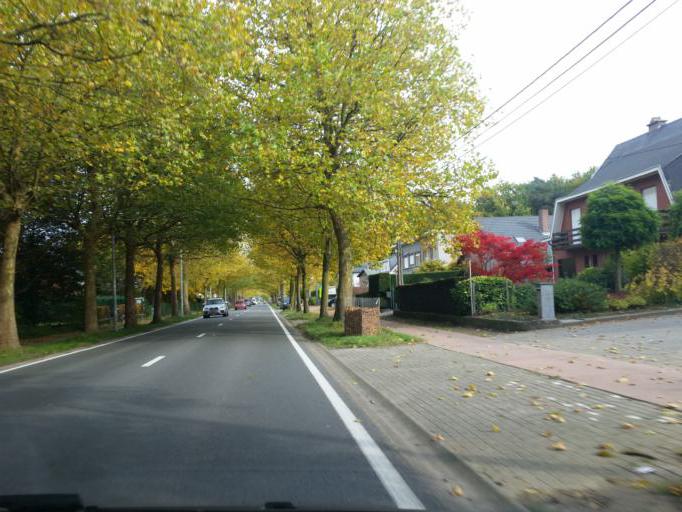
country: BE
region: Flanders
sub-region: Provincie Antwerpen
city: Putte
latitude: 51.0659
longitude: 4.6796
